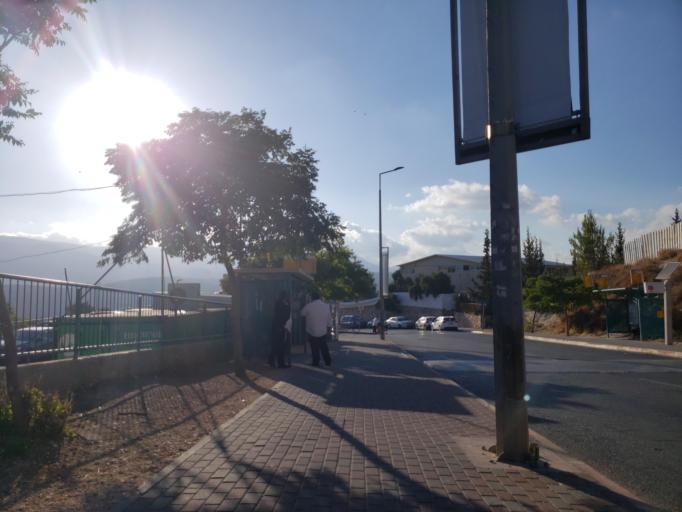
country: IL
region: Northern District
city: Safed
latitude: 32.9660
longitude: 35.4881
